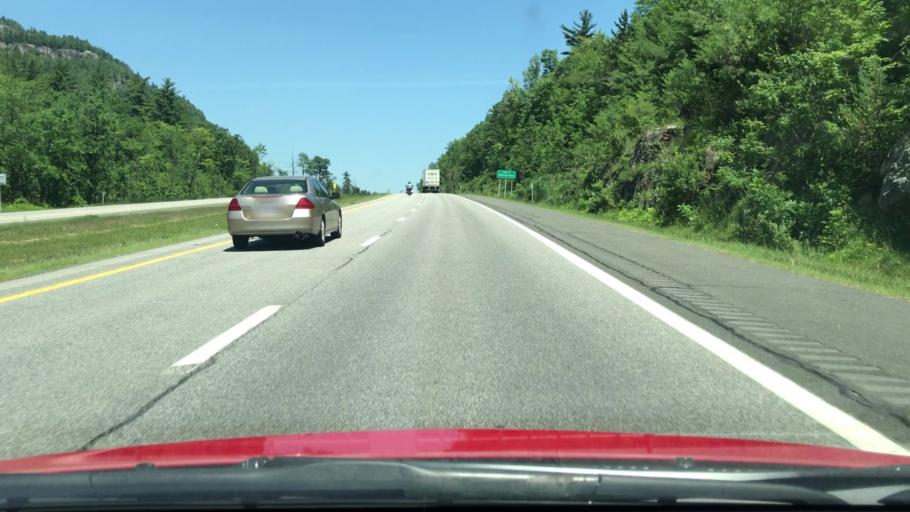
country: US
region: New York
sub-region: Essex County
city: Keeseville
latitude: 44.3941
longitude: -73.5023
